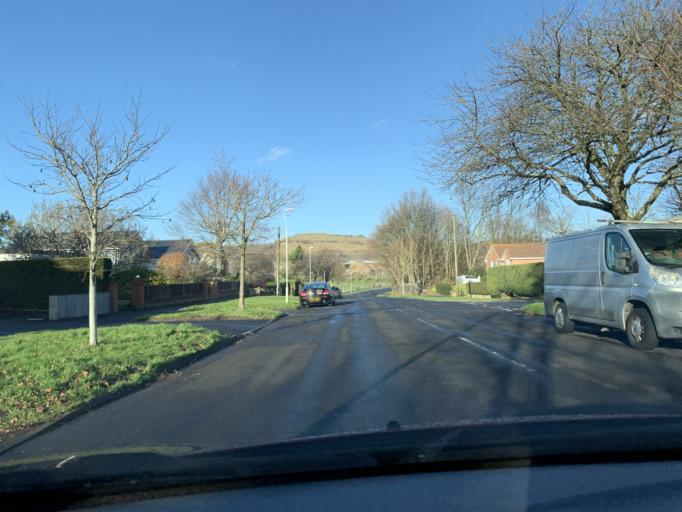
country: GB
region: England
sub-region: Kent
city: Folkestone
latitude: 51.0867
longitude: 1.1637
